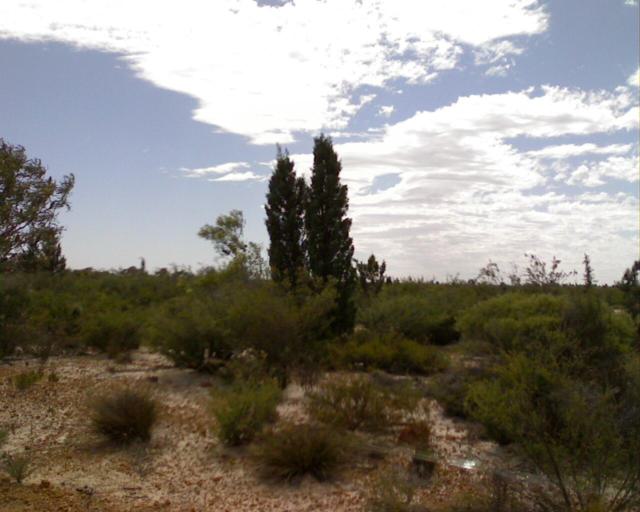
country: AU
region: Western Australia
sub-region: Moora
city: Moora
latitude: -30.0614
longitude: 115.6675
